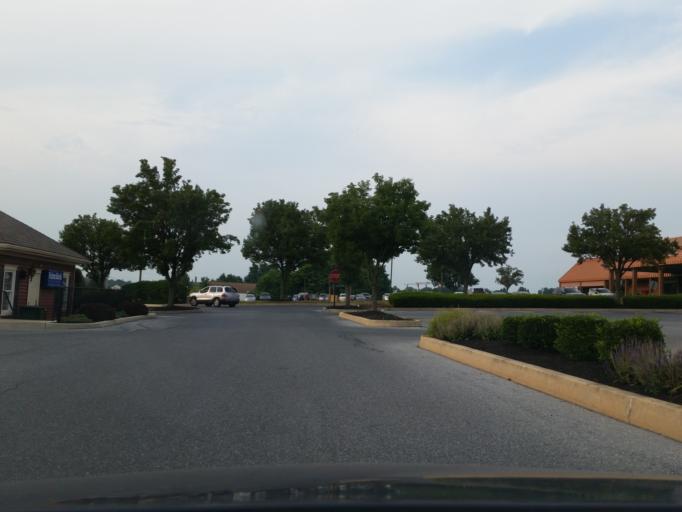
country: US
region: Pennsylvania
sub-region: Lebanon County
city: Lebanon South
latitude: 40.3110
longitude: -76.4241
